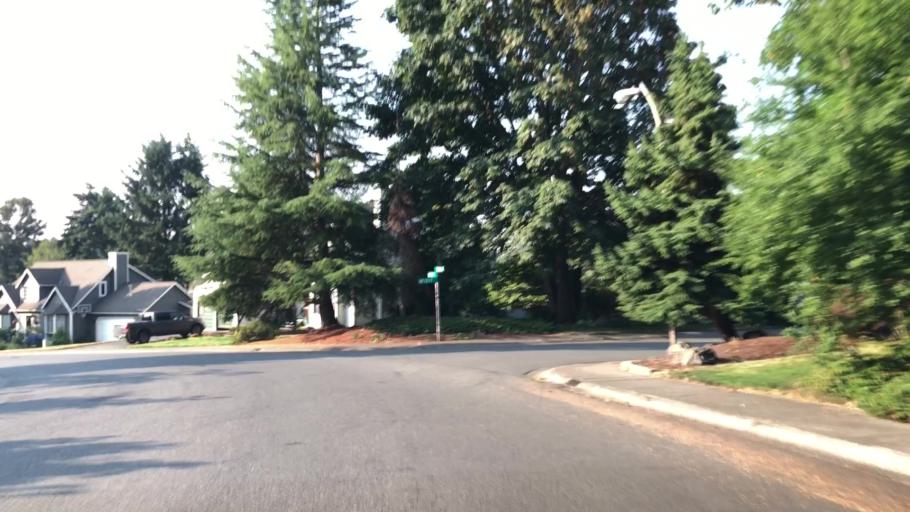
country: US
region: Washington
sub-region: King County
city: Cottage Lake
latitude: 47.7180
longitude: -122.1020
